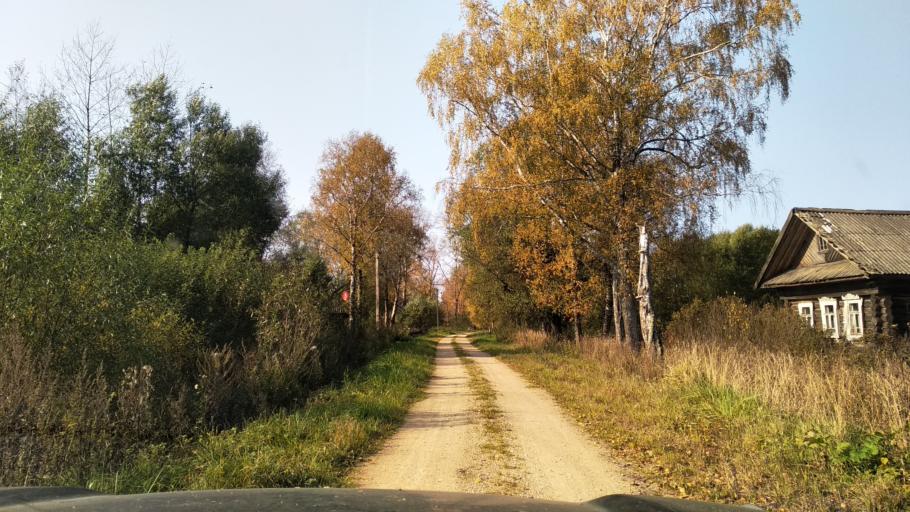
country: RU
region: Tverskaya
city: Krasnyy Kholm
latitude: 58.0328
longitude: 37.1875
